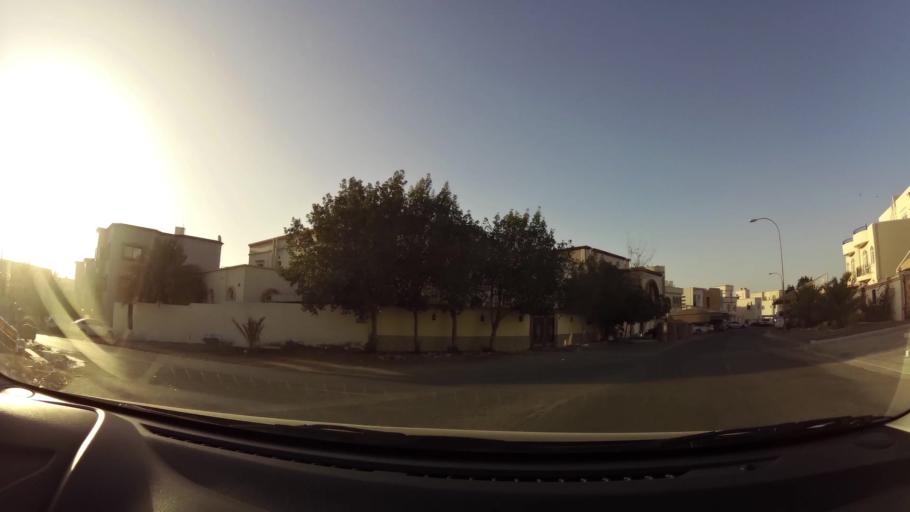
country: OM
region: Muhafazat Masqat
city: As Sib al Jadidah
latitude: 23.6065
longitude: 58.2229
